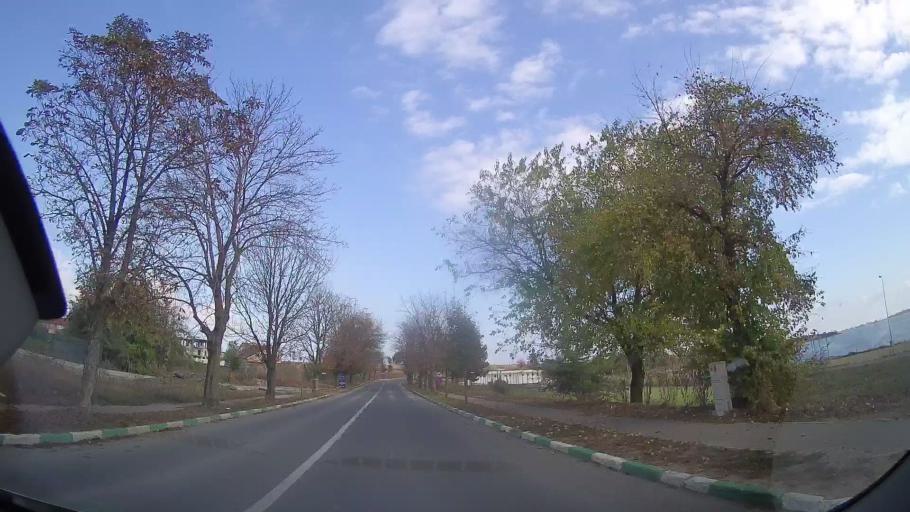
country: RO
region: Constanta
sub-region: Oras Techirghiol
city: Techirghiol
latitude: 44.0566
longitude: 28.6077
